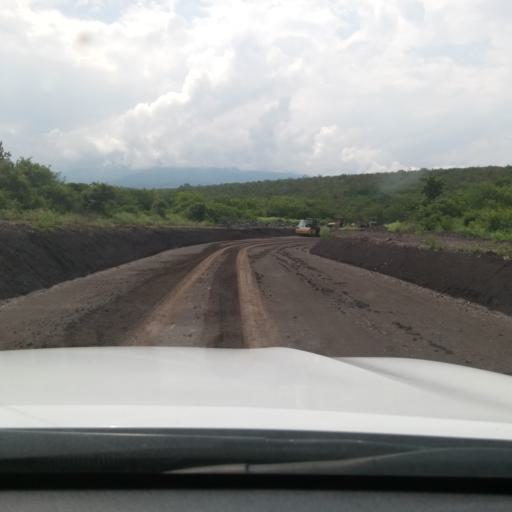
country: ET
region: Southern Nations, Nationalities, and People's Region
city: Arba Minch'
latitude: 6.3610
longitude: 37.2968
